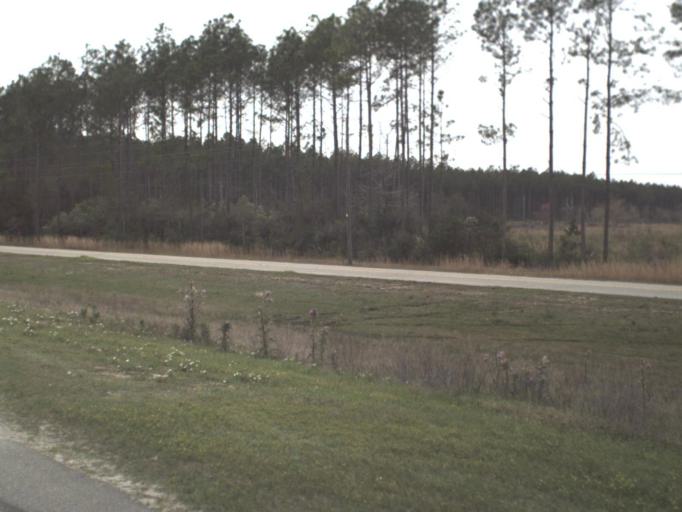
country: US
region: Florida
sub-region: Gulf County
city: Port Saint Joe
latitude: 29.8771
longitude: -85.2248
